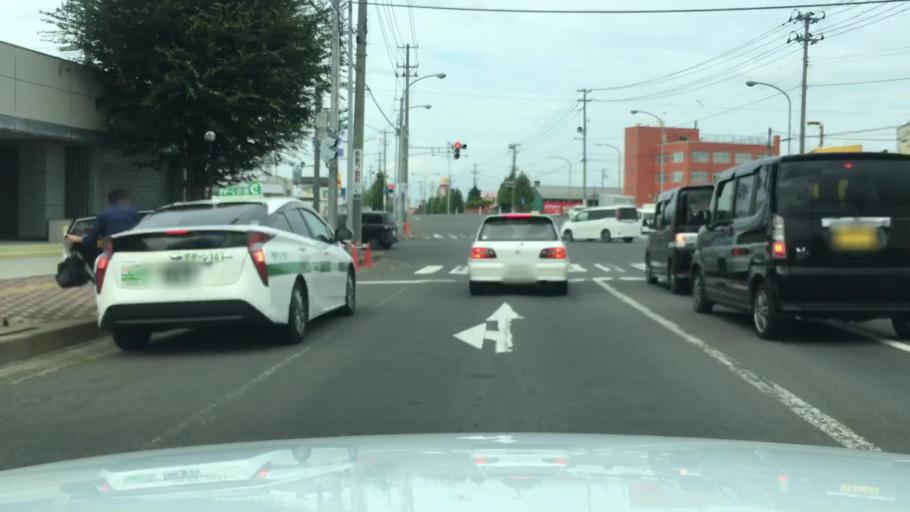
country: JP
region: Aomori
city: Hirosaki
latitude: 40.6096
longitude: 140.4810
